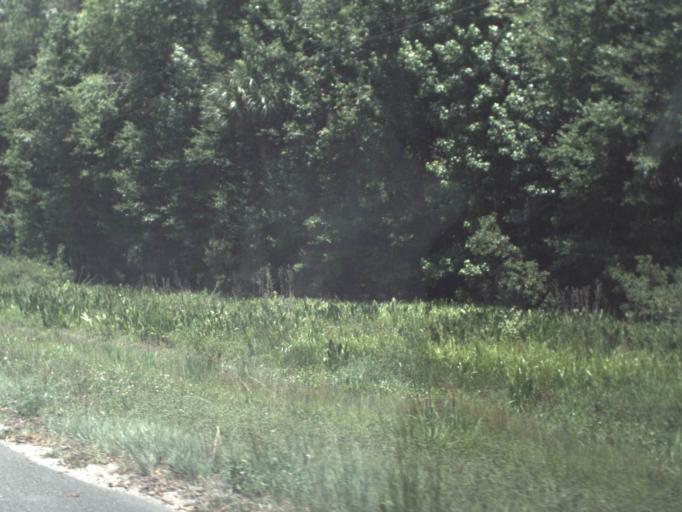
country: US
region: Florida
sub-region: Putnam County
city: Palatka
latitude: 29.5417
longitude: -81.7528
